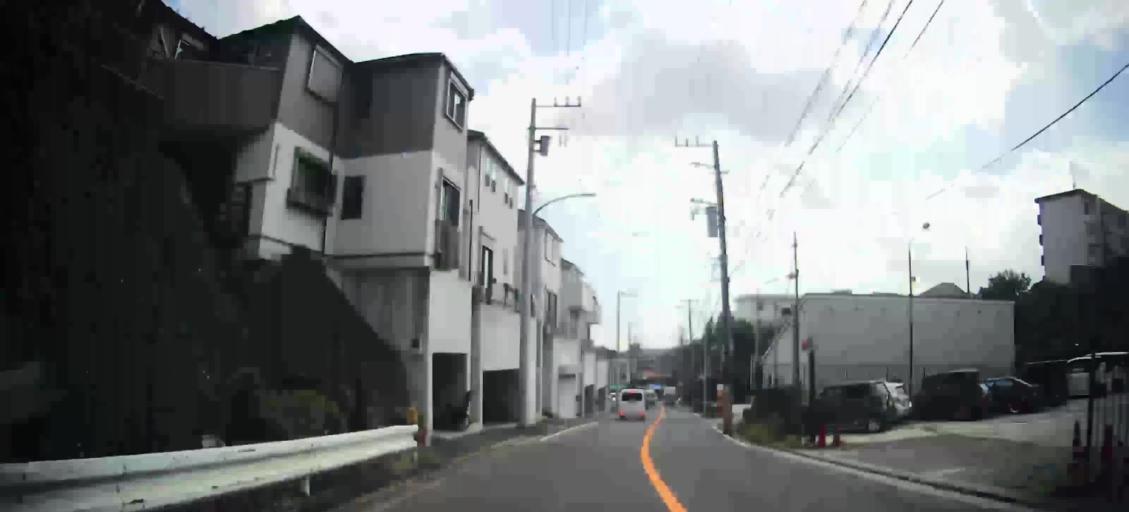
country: JP
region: Kanagawa
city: Yokohama
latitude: 35.4798
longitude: 139.5770
